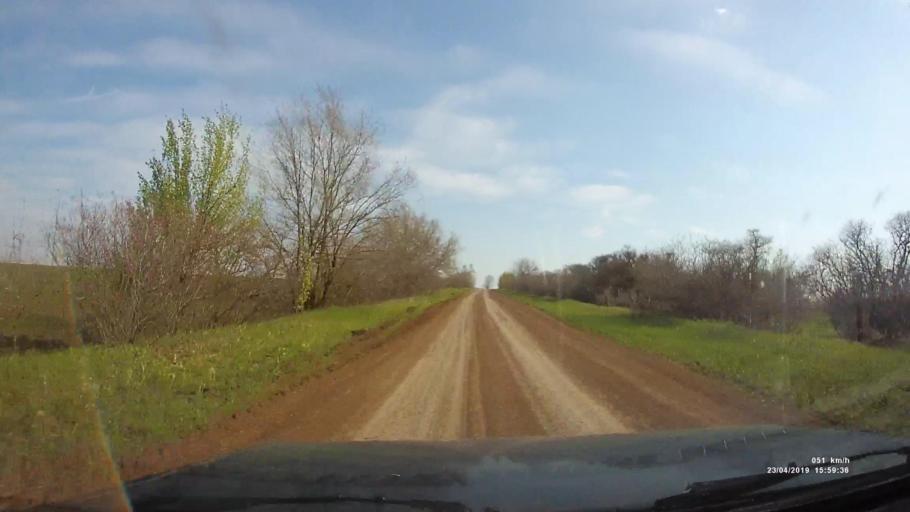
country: RU
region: Rostov
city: Remontnoye
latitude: 46.5156
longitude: 43.1096
